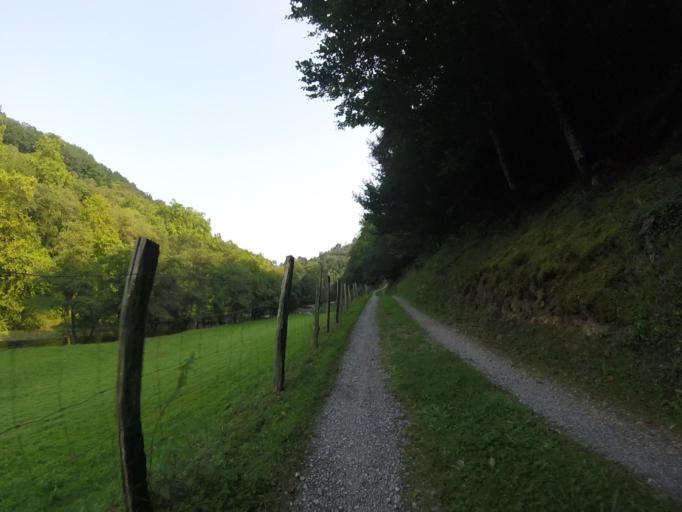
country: ES
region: Navarre
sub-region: Provincia de Navarra
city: Arano
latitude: 43.2258
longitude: -1.9326
